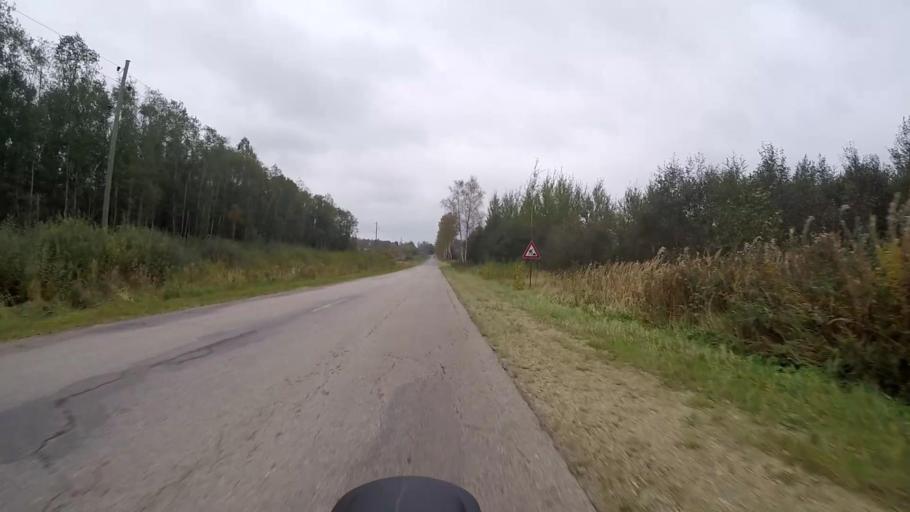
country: LV
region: Seja
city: Loja
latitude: 57.2589
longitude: 24.6372
